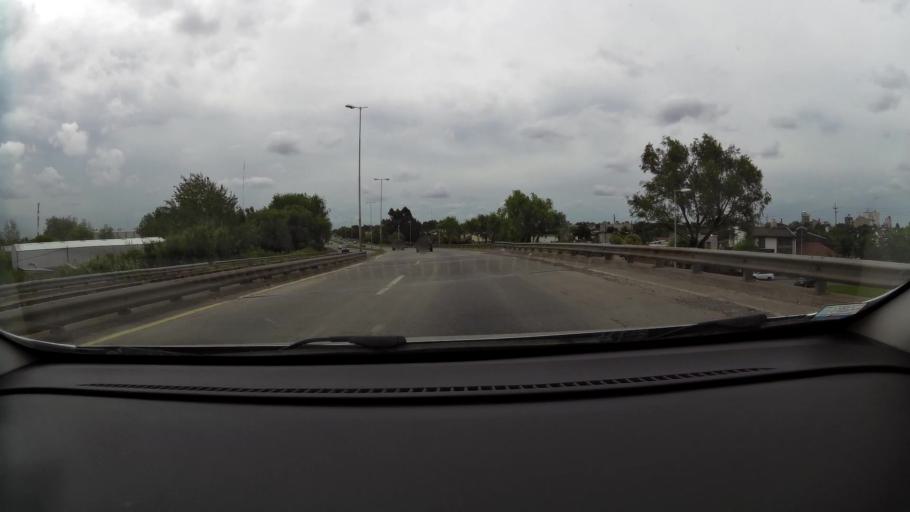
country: AR
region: Buenos Aires
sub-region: Partido de Campana
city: Campana
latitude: -34.1706
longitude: -58.9717
